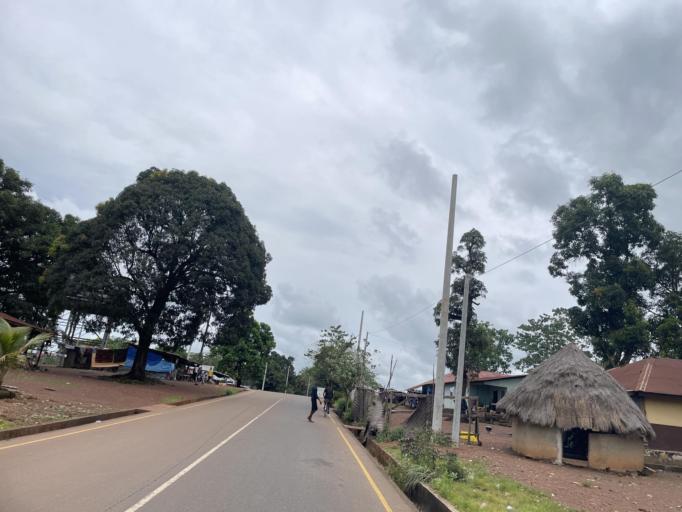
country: SL
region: Northern Province
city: Kambia
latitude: 9.1277
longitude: -12.9087
